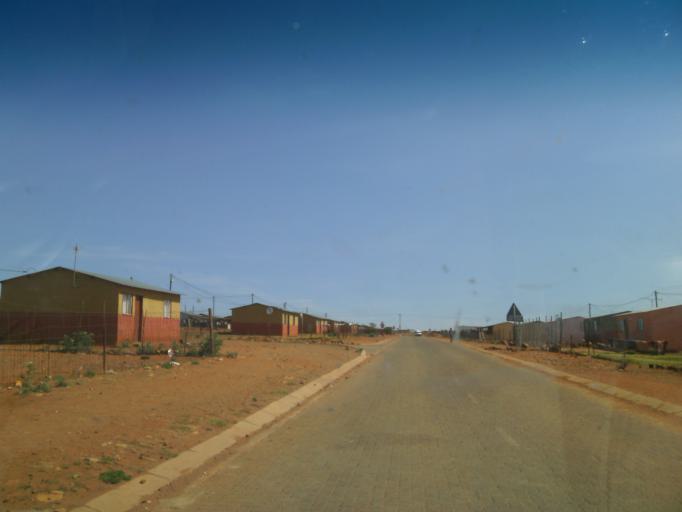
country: ZA
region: Northern Cape
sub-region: Frances Baard District Municipality
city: Barkly West
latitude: -28.5201
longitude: 24.5011
